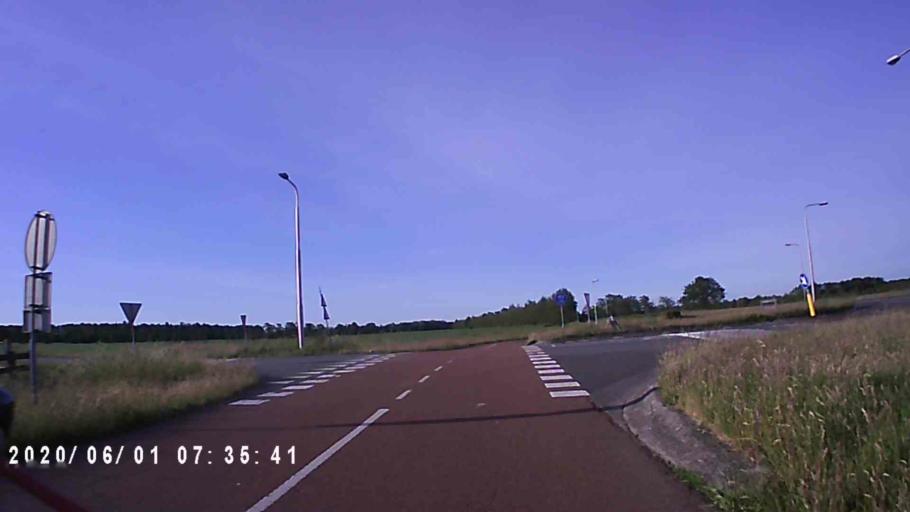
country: NL
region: Friesland
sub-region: Gemeente Dantumadiel
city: Damwald
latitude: 53.3055
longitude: 5.9946
